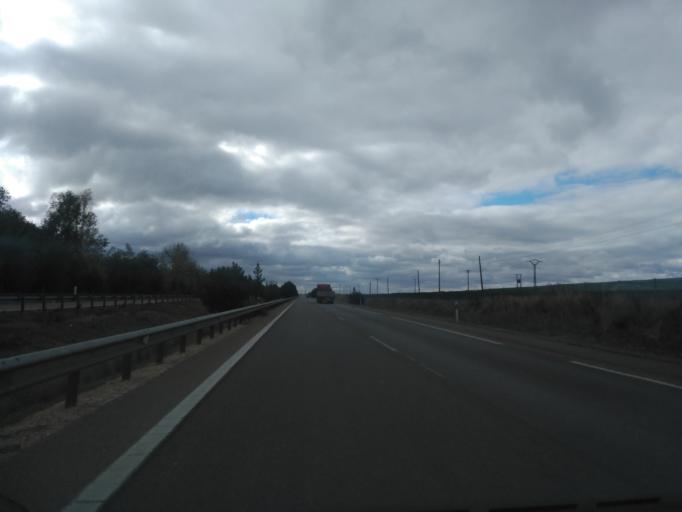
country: ES
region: Castille and Leon
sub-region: Provincia de Valladolid
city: Cubillas de Santa Marta
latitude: 41.7951
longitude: -4.5988
